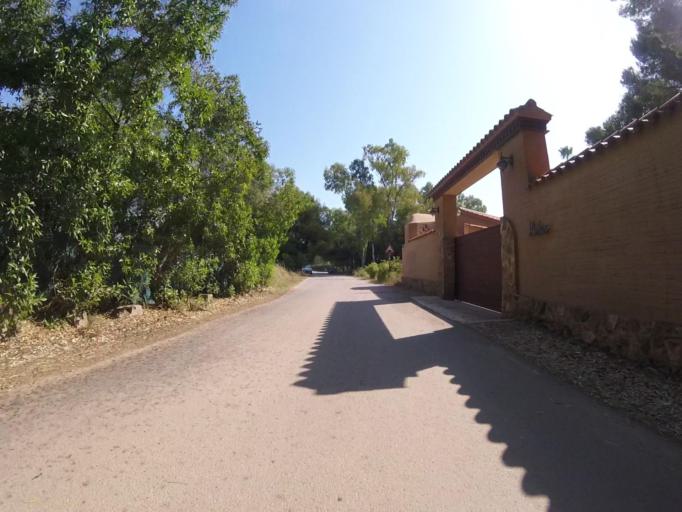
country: ES
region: Valencia
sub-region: Provincia de Castello
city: Orpesa/Oropesa del Mar
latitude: 40.1298
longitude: 0.1616
